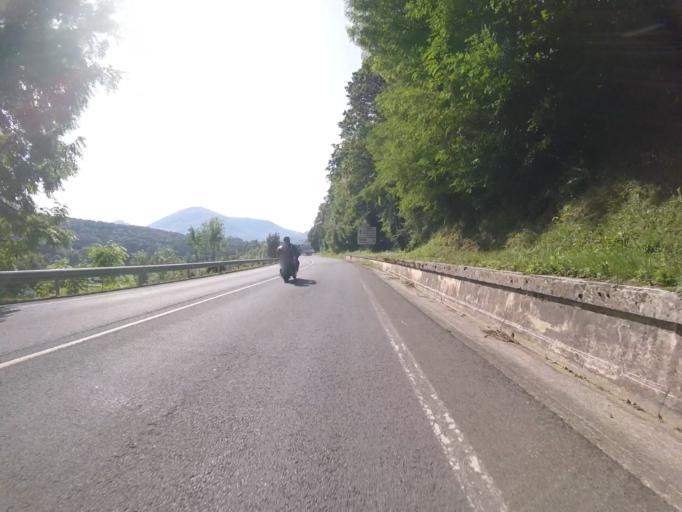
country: ES
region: Navarre
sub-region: Provincia de Navarra
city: Zugarramurdi
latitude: 43.1997
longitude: -1.4847
